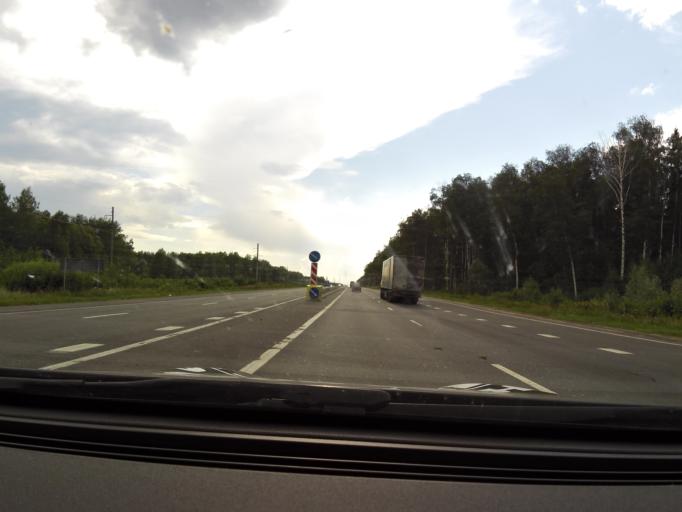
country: RU
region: Nizjnij Novgorod
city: Smolino
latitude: 56.2817
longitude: 43.0902
